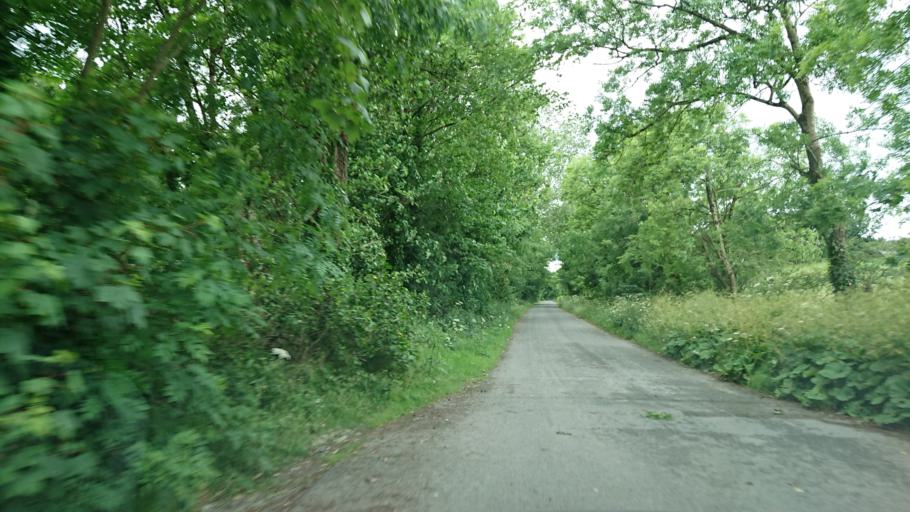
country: IE
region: Munster
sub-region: Waterford
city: Waterford
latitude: 52.2183
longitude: -7.1286
